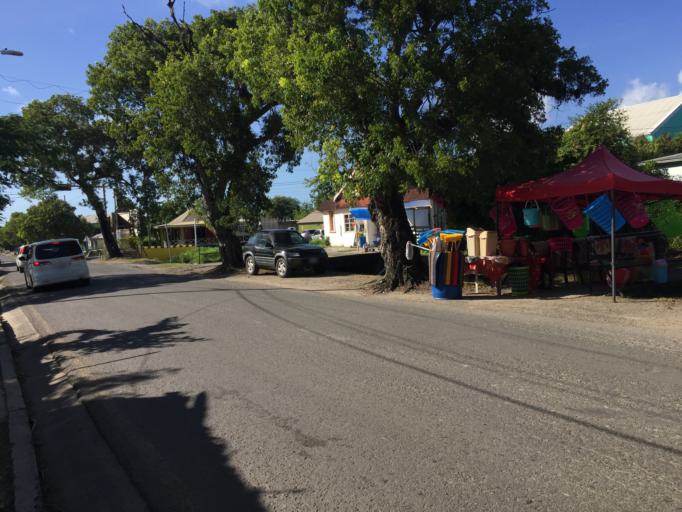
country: AG
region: Saint John
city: Saint John's
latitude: 17.1259
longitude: -61.8442
